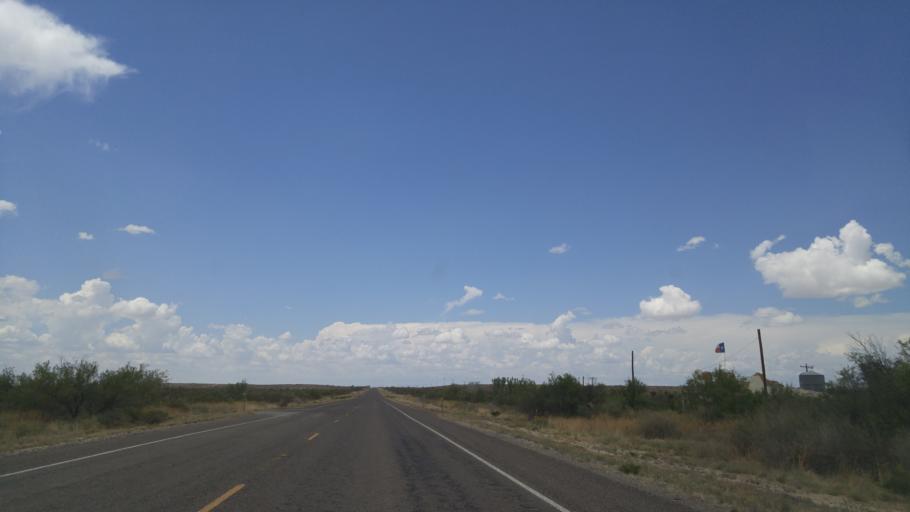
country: US
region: Texas
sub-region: Brewster County
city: Alpine
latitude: 29.6080
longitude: -103.5648
